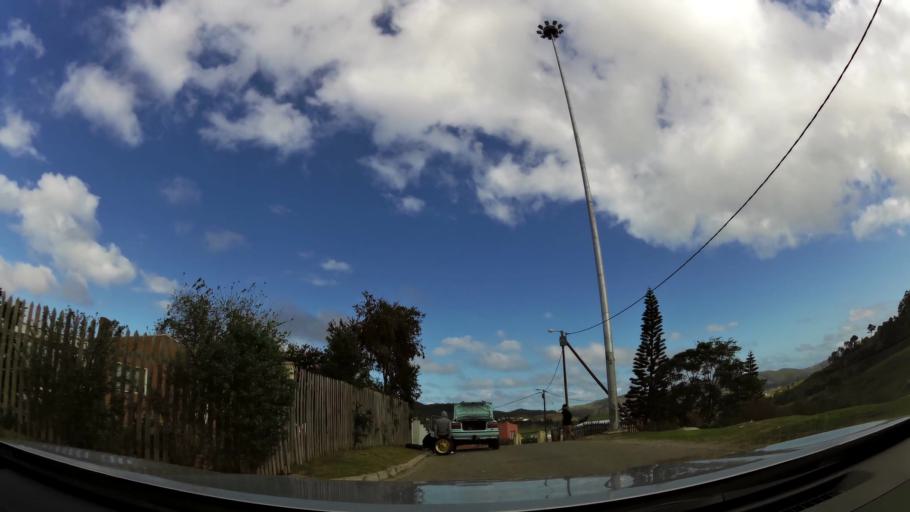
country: ZA
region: Western Cape
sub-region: Eden District Municipality
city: Knysna
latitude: -34.0531
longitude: 23.0945
